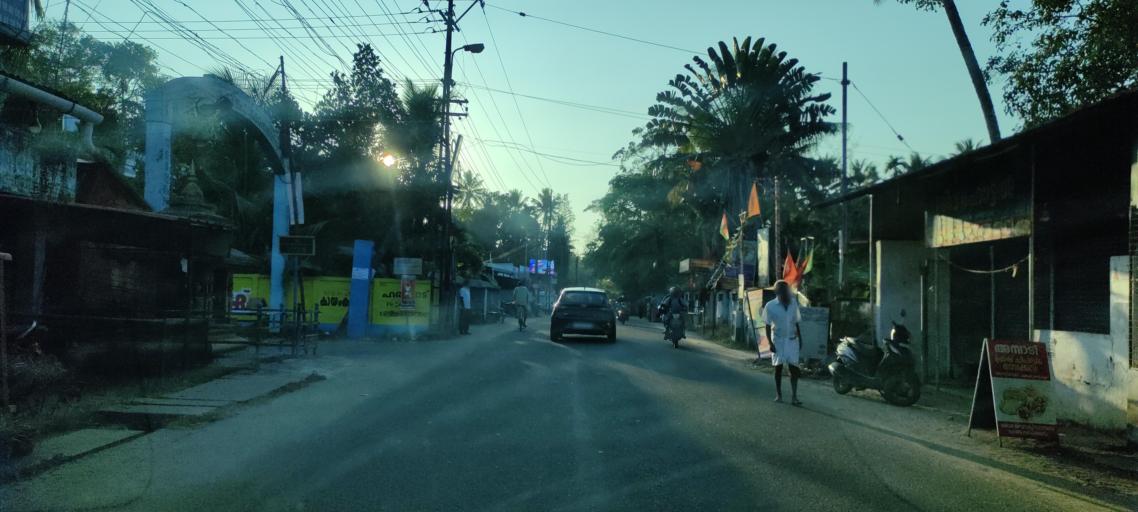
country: IN
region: Kerala
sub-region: Alappuzha
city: Kayankulam
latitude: 9.1768
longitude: 76.4816
